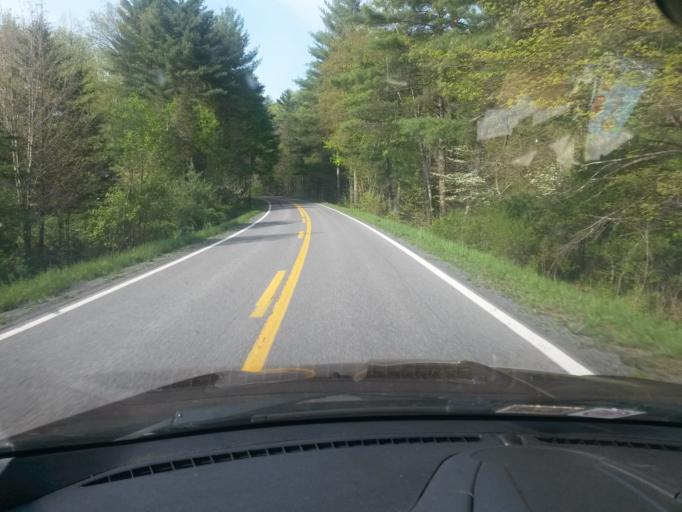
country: US
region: West Virginia
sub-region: Pocahontas County
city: Marlinton
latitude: 38.0296
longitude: -80.0407
